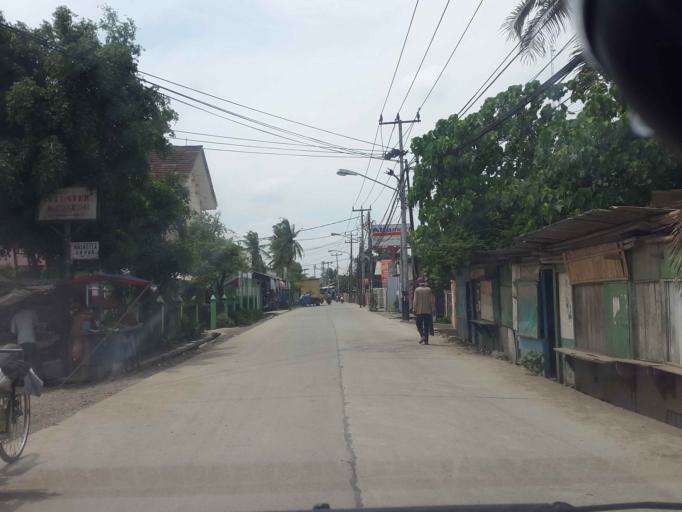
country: ID
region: West Java
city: Teluknaga
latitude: -6.1232
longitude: 106.6242
